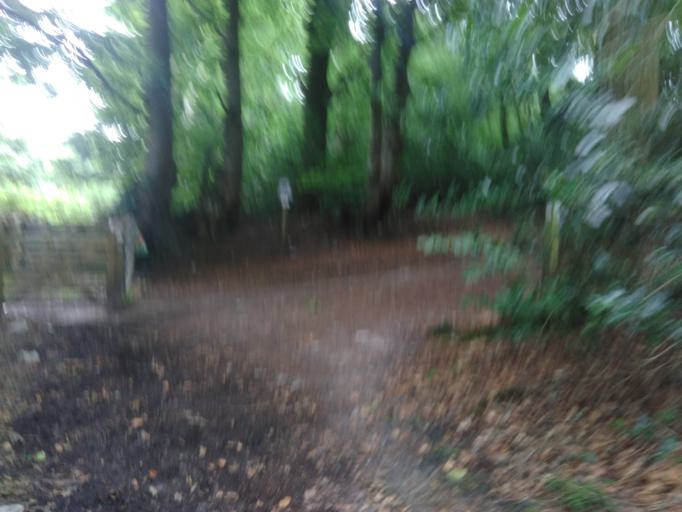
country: GB
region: England
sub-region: Devon
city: Uffculme
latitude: 50.9458
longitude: -3.2349
